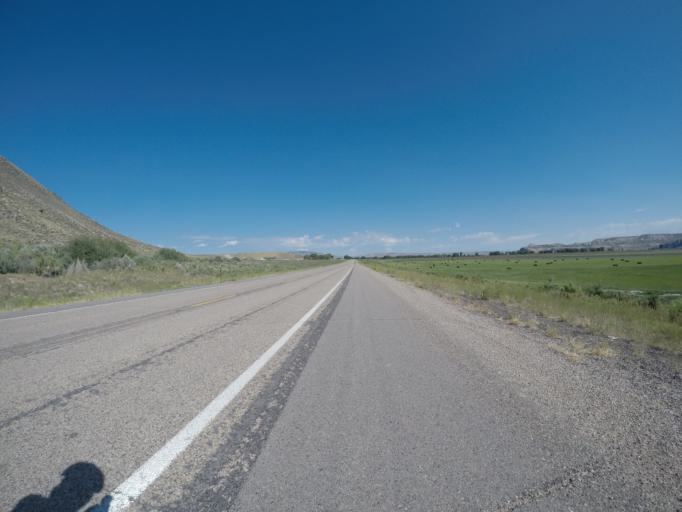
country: US
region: Wyoming
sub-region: Sublette County
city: Marbleton
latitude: 42.2050
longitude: -110.1817
